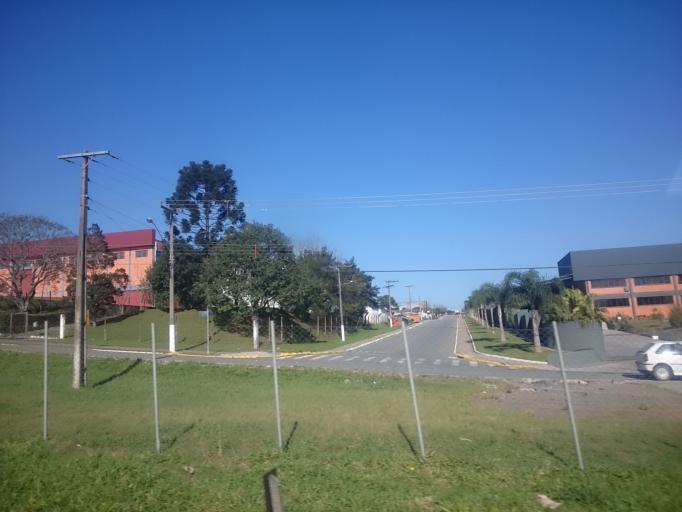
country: BR
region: Parana
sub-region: Rio Negro
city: Rio Negro
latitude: -26.0815
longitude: -49.7721
